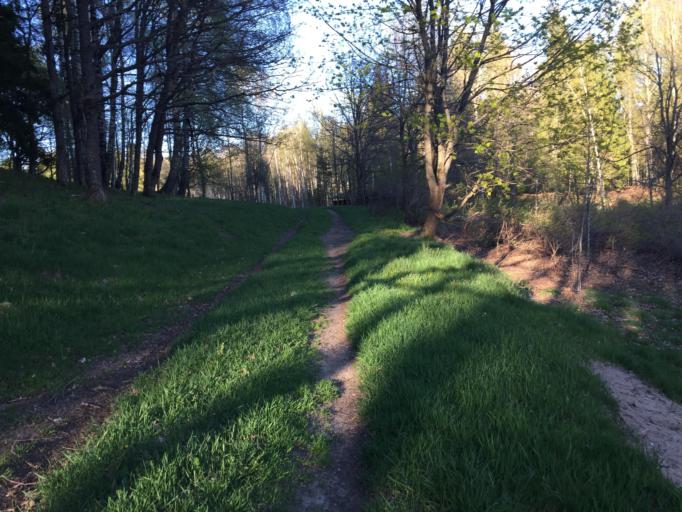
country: LV
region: Vecpiebalga
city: Vecpiebalga
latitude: 56.8684
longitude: 25.9629
